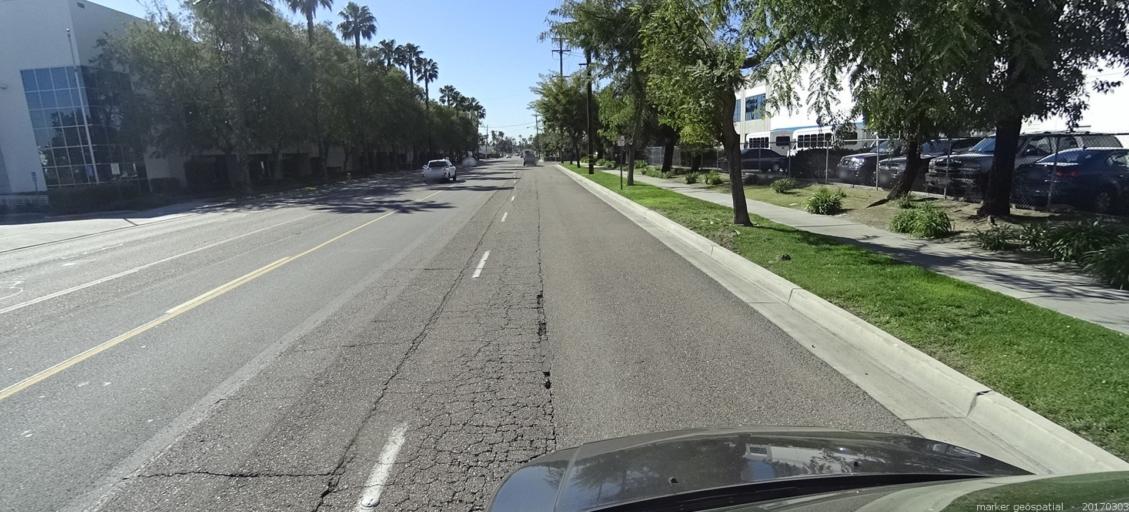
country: US
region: California
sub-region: Orange County
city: Anaheim
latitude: 33.8519
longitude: -117.9200
